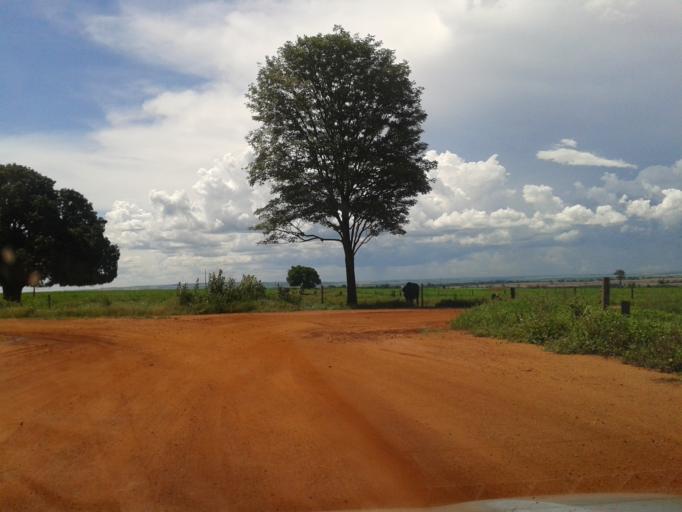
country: BR
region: Minas Gerais
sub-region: Capinopolis
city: Capinopolis
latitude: -18.7038
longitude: -49.7735
